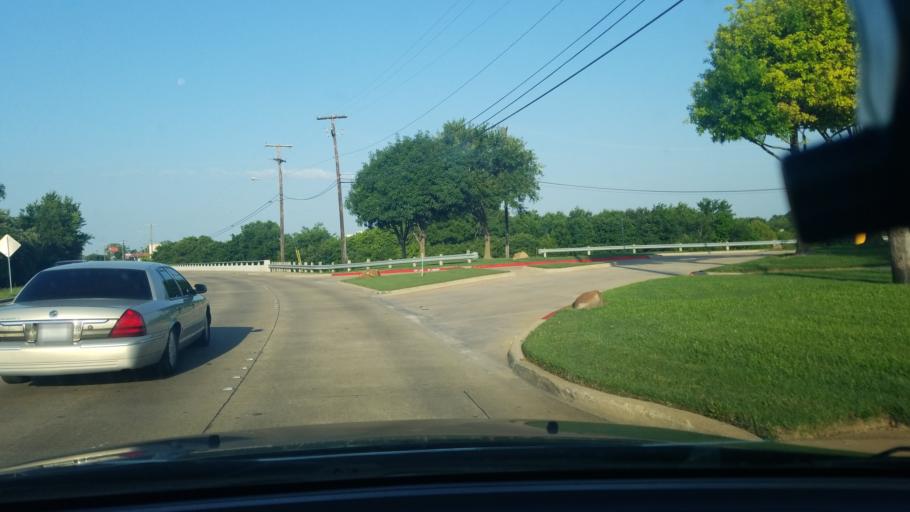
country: US
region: Texas
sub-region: Dallas County
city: Mesquite
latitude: 32.8014
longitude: -96.6298
